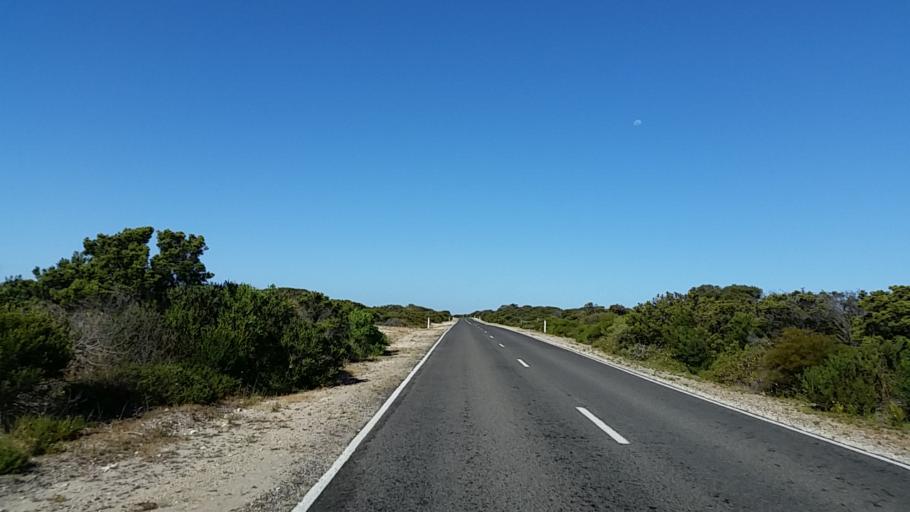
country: AU
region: South Australia
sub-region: Yorke Peninsula
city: Honiton
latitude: -35.2644
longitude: 136.9517
